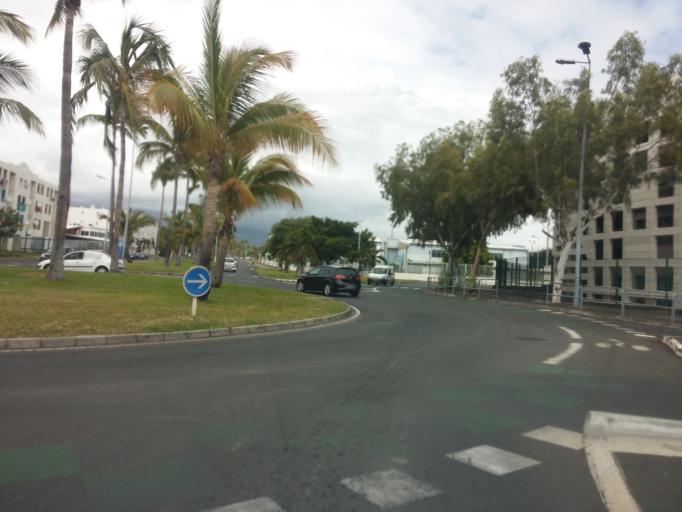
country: RE
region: Reunion
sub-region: Reunion
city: Le Port
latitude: -20.9422
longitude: 55.2918
